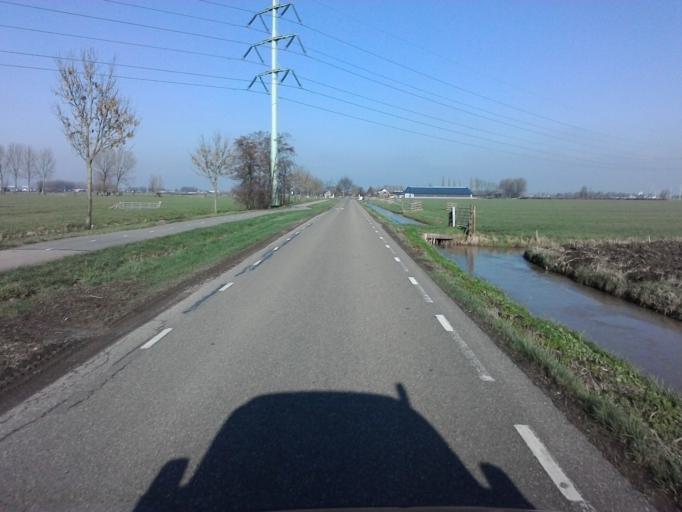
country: NL
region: South Holland
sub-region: Gemeente Gorinchem
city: Gorinchem
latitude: 51.8593
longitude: 4.9632
